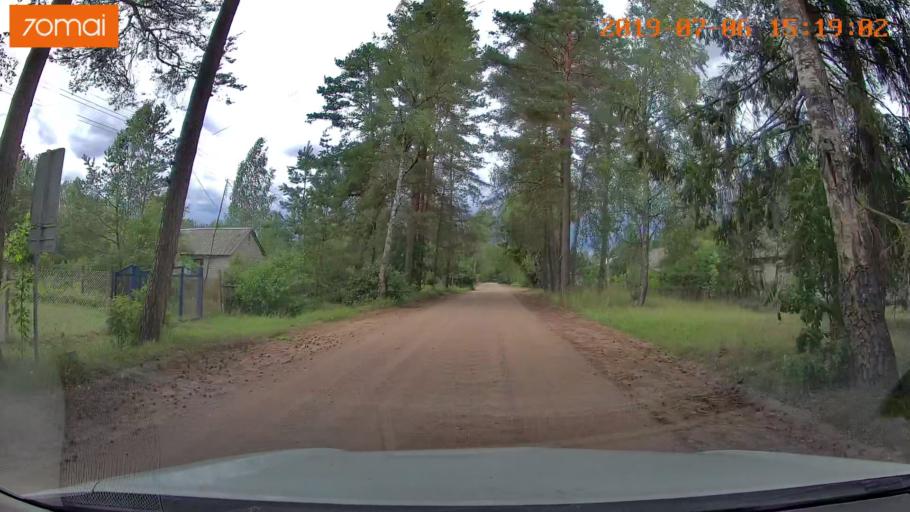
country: BY
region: Minsk
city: Ivyanyets
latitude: 53.9946
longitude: 26.6485
